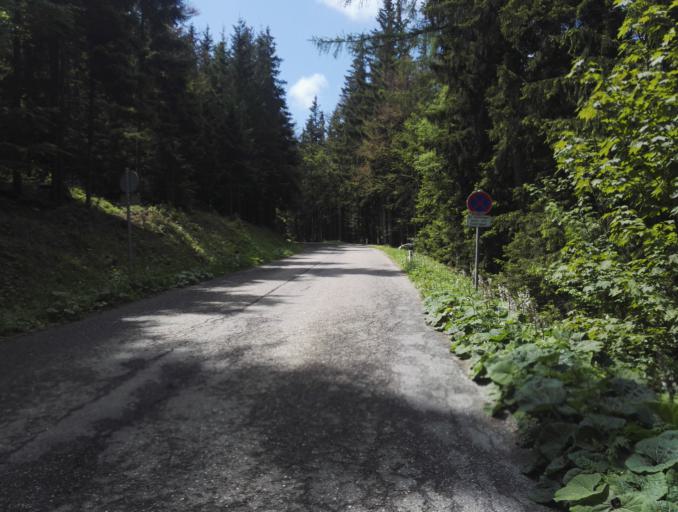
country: AT
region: Styria
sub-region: Politischer Bezirk Weiz
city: Stenzengreith
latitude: 47.2070
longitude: 15.4868
